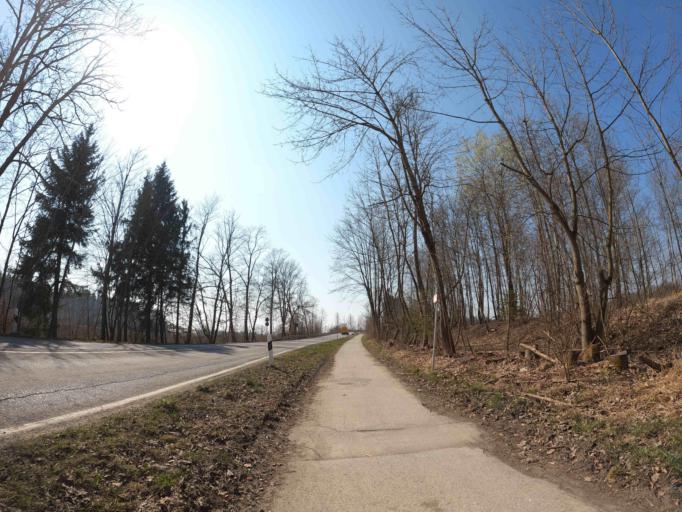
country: DE
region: Bavaria
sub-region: Upper Bavaria
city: Starnberg
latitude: 48.0011
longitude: 11.3790
